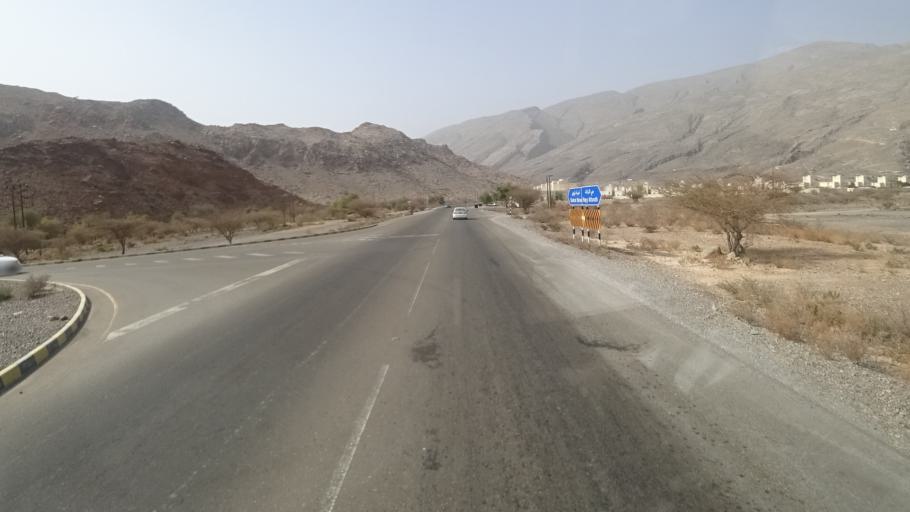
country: OM
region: Muhafazat ad Dakhiliyah
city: Nizwa
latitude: 22.9898
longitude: 57.5850
